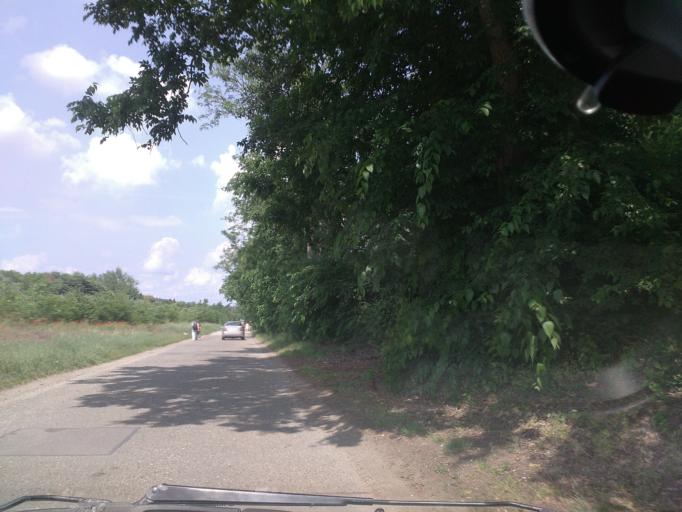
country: HU
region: Pest
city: Veresegyhaz
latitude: 47.6433
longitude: 19.2681
